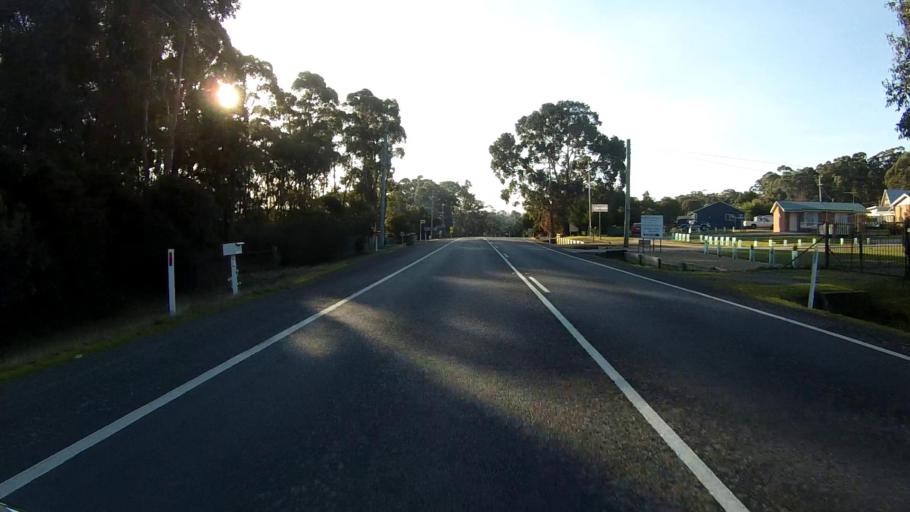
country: AU
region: Tasmania
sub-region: Clarence
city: Sandford
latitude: -43.0388
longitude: 147.8652
